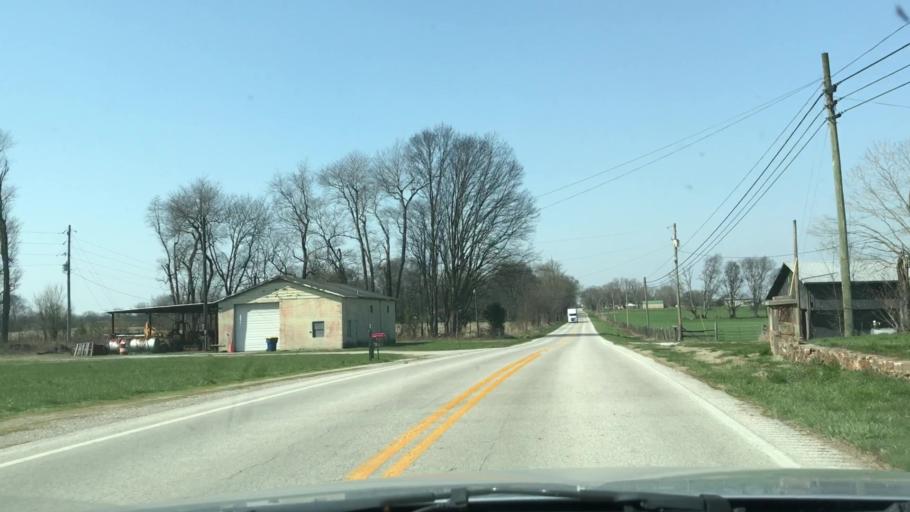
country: US
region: Kentucky
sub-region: Edmonson County
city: Brownsville
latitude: 37.0922
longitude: -86.1343
